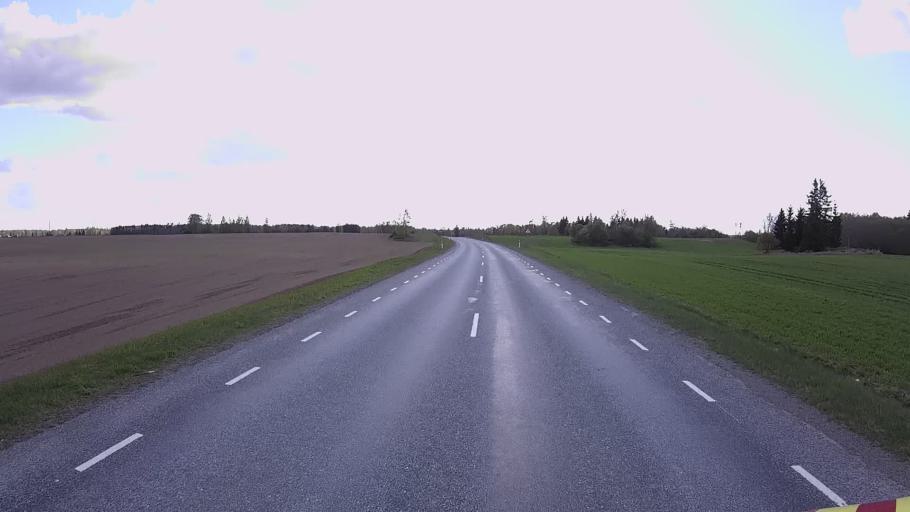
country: EE
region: Jogevamaa
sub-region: Poltsamaa linn
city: Poltsamaa
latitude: 58.6854
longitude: 26.0881
